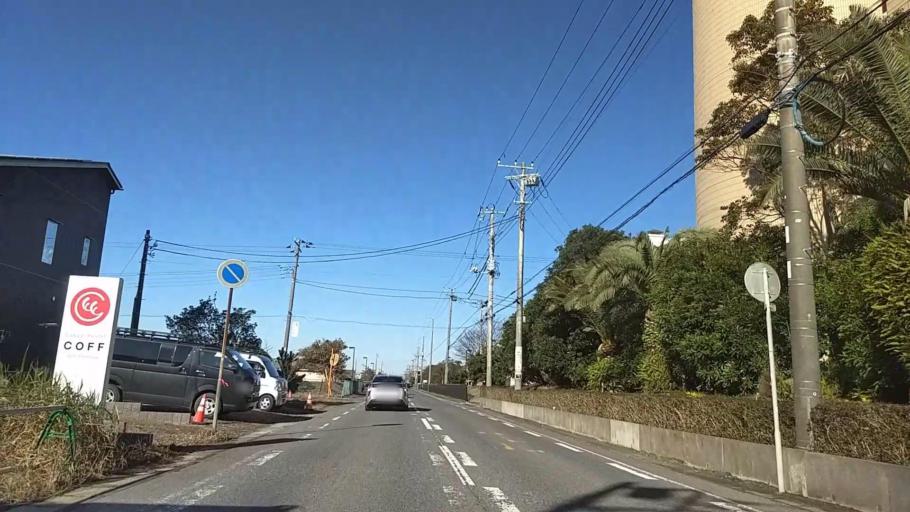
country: JP
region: Chiba
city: Mobara
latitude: 35.3629
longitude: 140.3880
